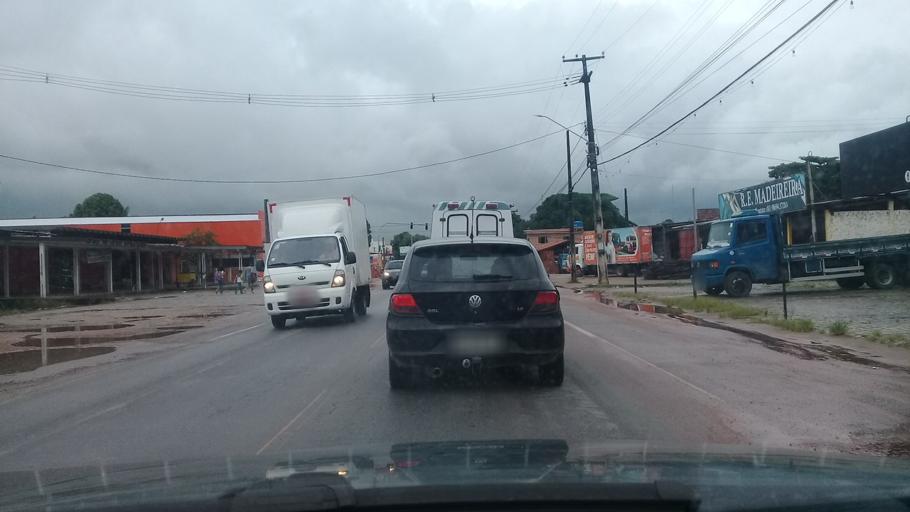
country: BR
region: Pernambuco
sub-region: Igarassu
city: Igarassu
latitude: -7.8247
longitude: -34.9103
